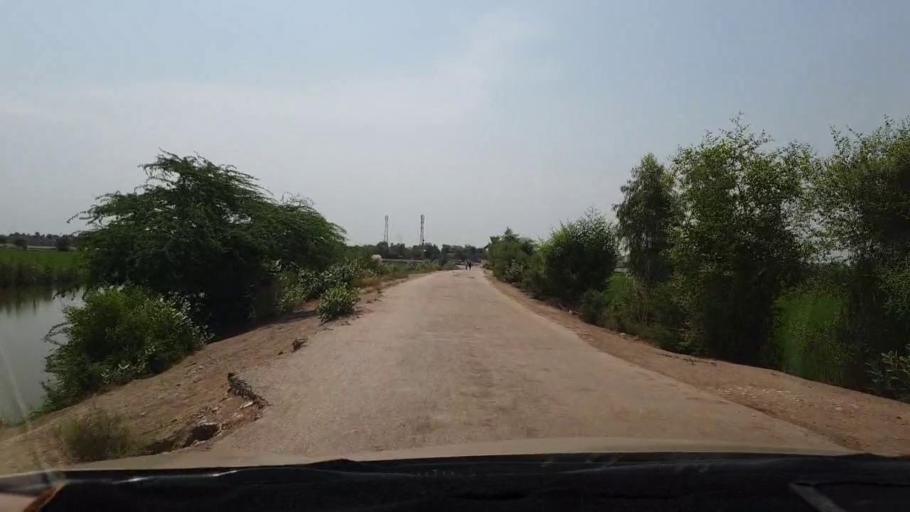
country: PK
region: Sindh
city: Larkana
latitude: 27.6231
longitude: 68.2754
